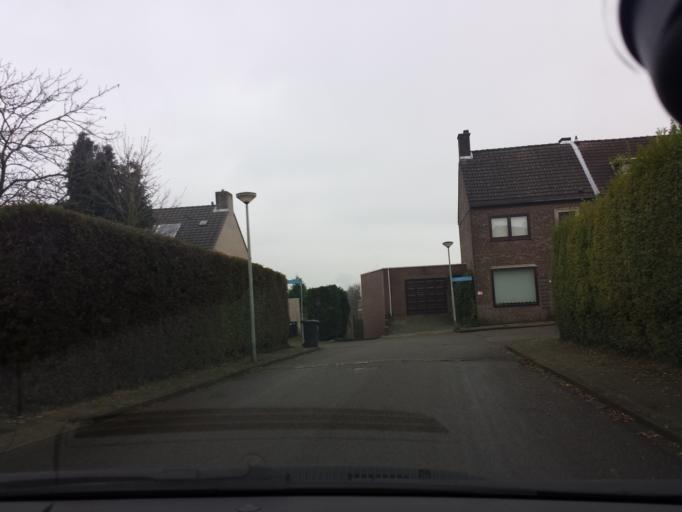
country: NL
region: Limburg
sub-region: Gemeente Kerkrade
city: Kerkrade
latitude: 50.8897
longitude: 6.0630
